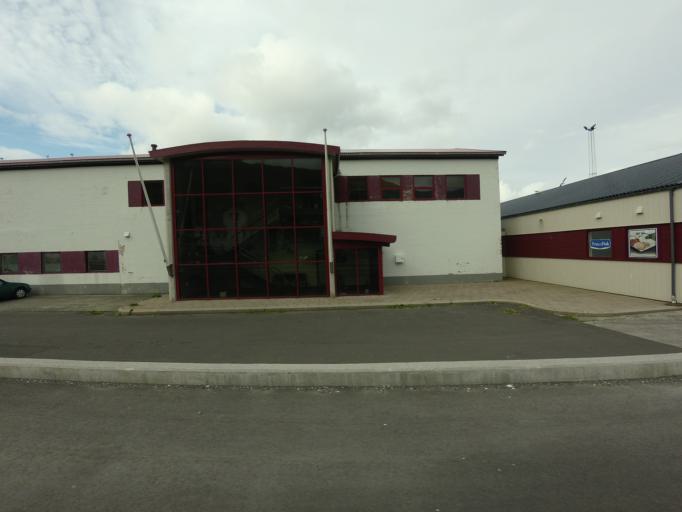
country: FO
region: Eysturoy
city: Eystur
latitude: 62.2109
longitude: -6.7076
